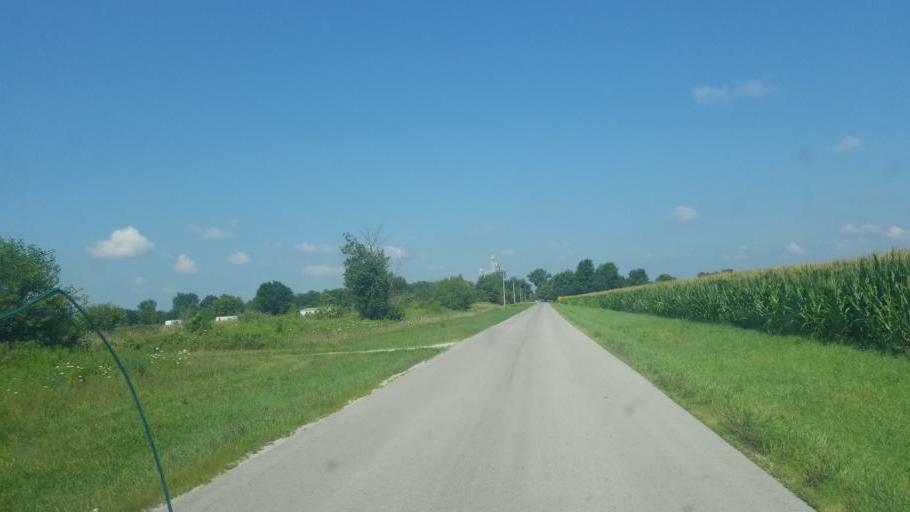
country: US
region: Ohio
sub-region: Hardin County
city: Ada
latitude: 40.6783
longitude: -83.7345
